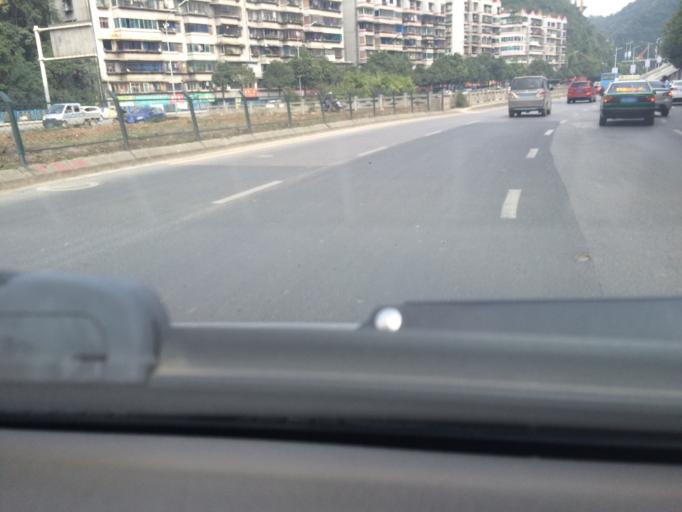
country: CN
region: Guizhou Sheng
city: Guiyang
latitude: 26.5847
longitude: 106.6772
